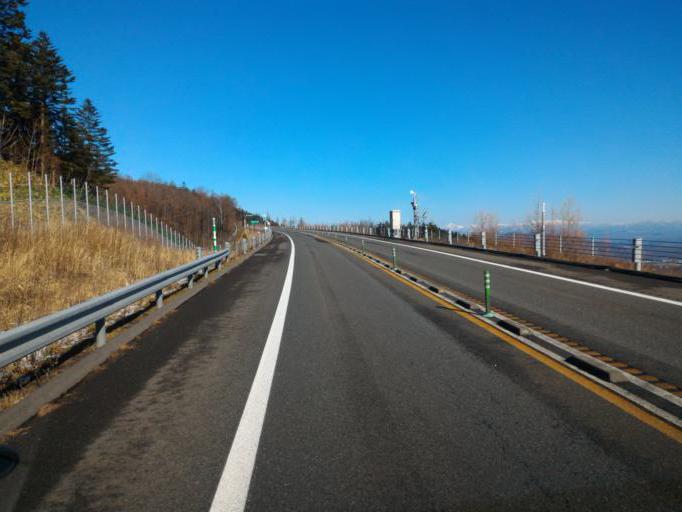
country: JP
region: Hokkaido
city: Otofuke
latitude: 43.0476
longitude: 142.7842
